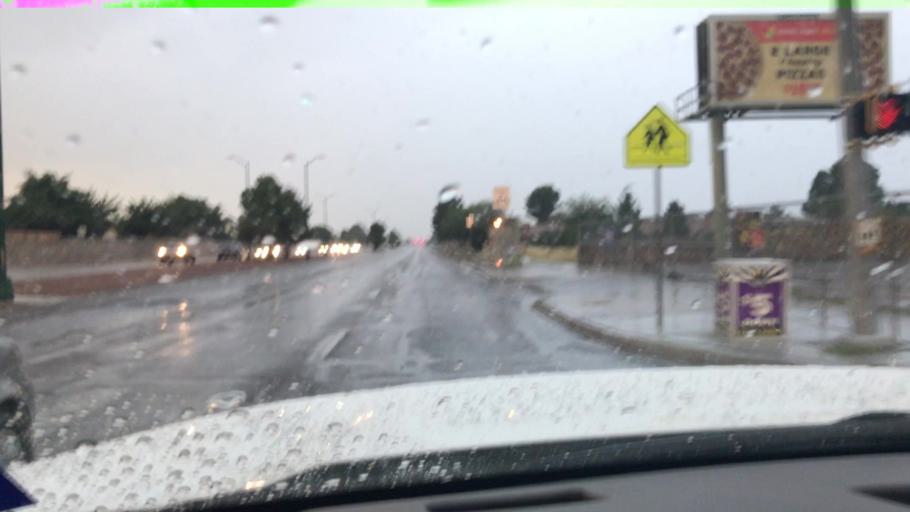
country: US
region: Texas
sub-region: El Paso County
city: Fort Bliss
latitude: 31.7915
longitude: -106.3234
